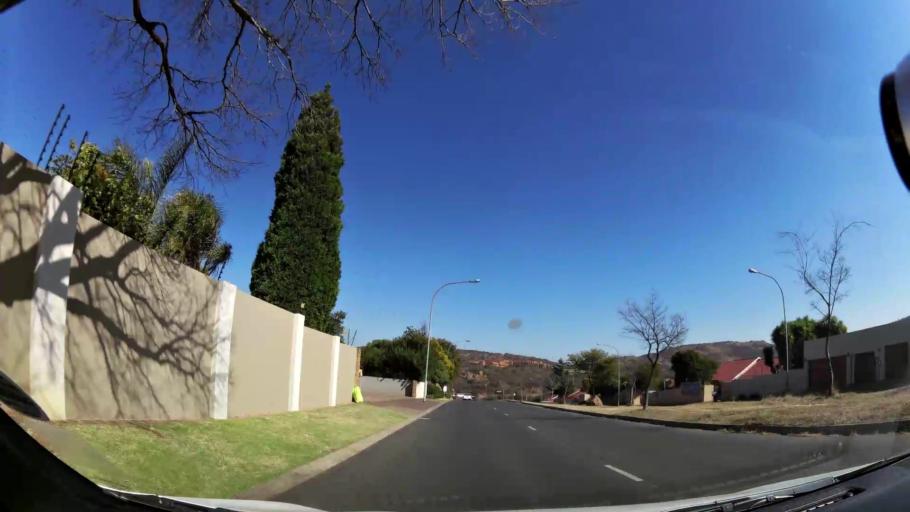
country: ZA
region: Gauteng
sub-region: City of Johannesburg Metropolitan Municipality
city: Johannesburg
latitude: -26.2894
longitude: 28.0461
